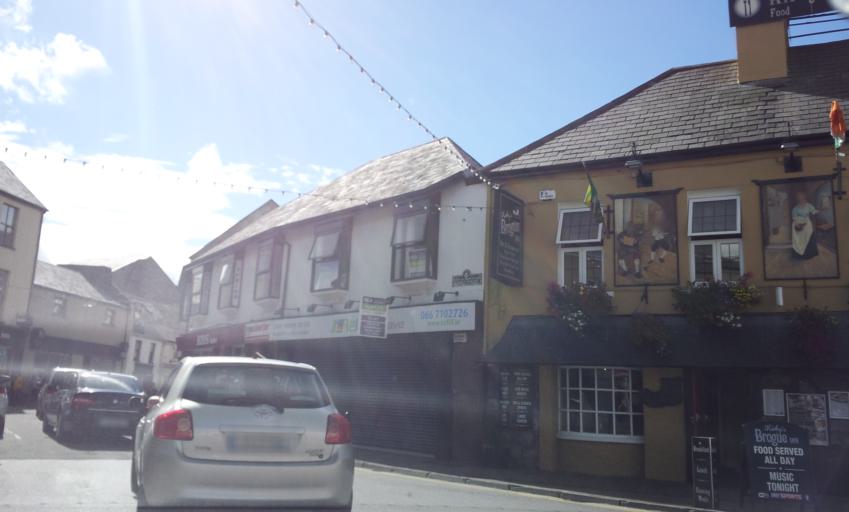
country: IE
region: Munster
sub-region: Ciarrai
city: Tralee
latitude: 52.2704
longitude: -9.7082
